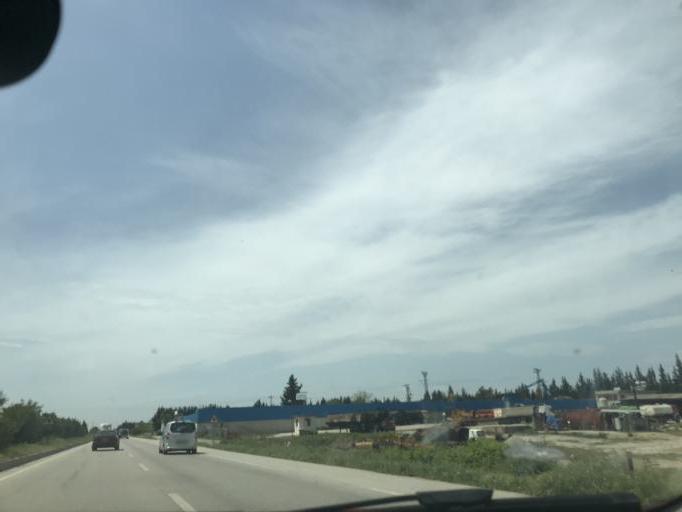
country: TR
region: Adana
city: Yakapinar
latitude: 36.9709
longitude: 35.5255
